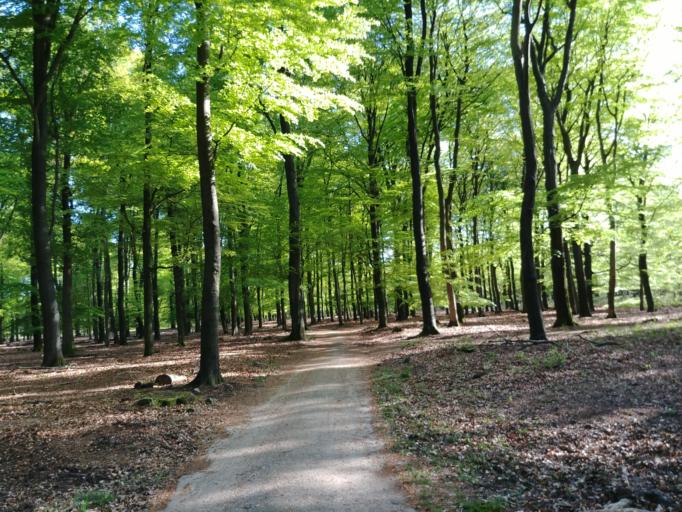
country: NL
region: Gelderland
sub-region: Gemeente Apeldoorn
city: Apeldoorn
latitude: 52.2419
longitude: 5.8838
